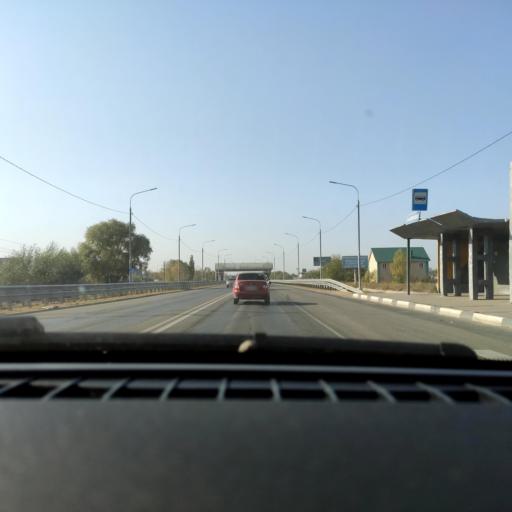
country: RU
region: Voronezj
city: Somovo
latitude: 51.6911
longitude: 39.3658
